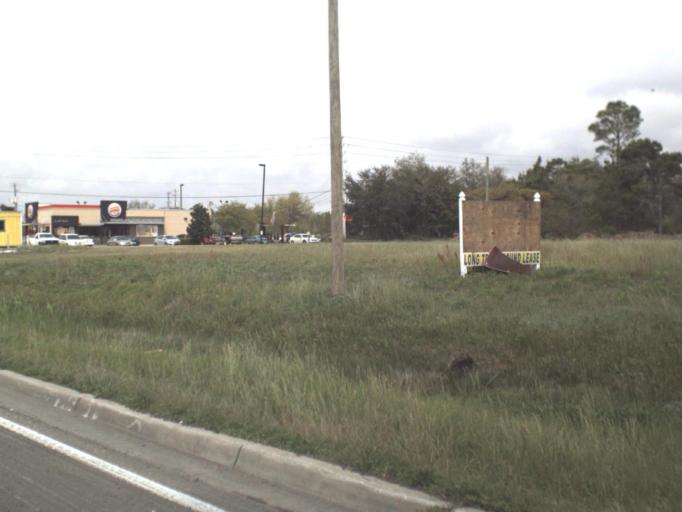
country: US
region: Florida
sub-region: Santa Rosa County
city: Navarre
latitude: 30.4016
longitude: -86.8623
